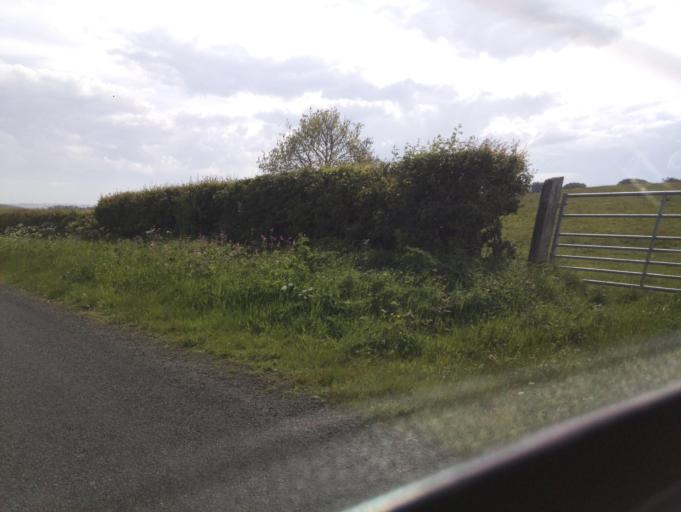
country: GB
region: England
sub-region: Northumberland
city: Alnwick
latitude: 55.4499
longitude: -1.7109
